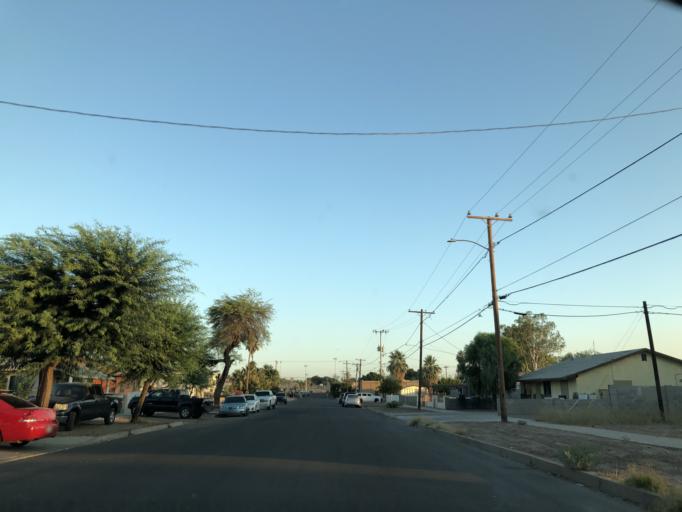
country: US
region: Arizona
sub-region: Yuma County
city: Yuma
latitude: 32.7232
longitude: -114.6308
